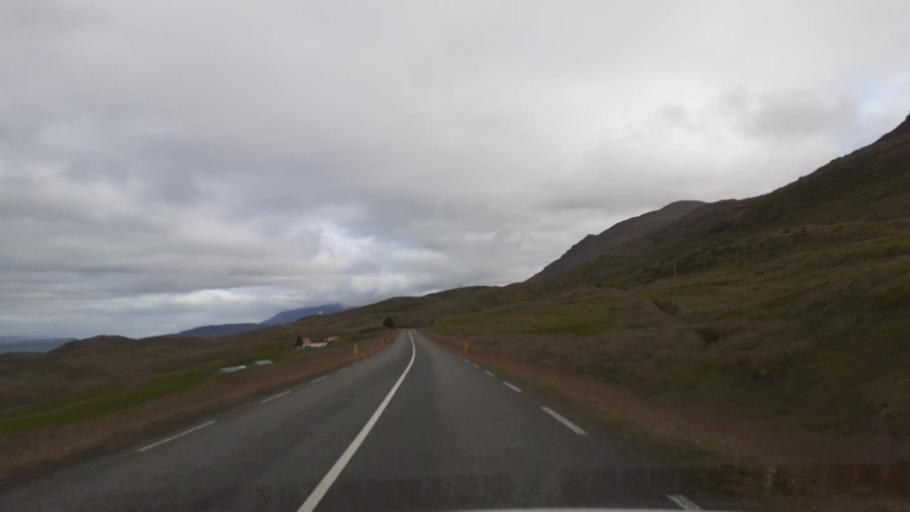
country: IS
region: Northeast
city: Akureyri
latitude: 65.8169
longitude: -18.0484
